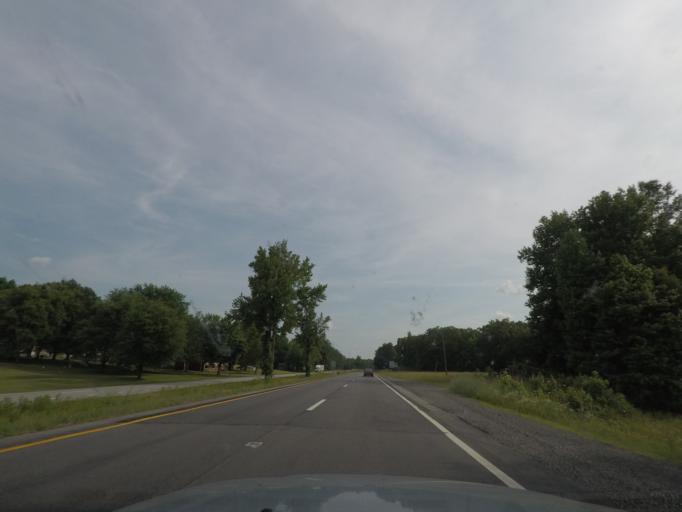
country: US
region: Virginia
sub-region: Mecklenburg County
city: Chase City
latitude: 36.9369
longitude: -78.5053
